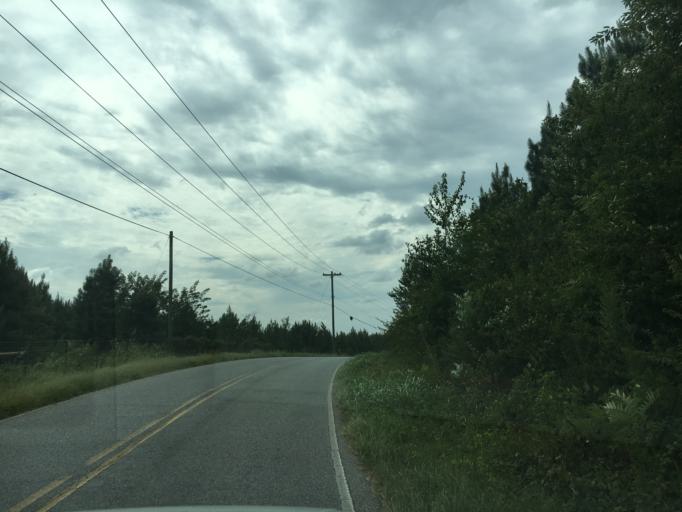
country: US
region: South Carolina
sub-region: Greenville County
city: Greer
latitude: 34.9255
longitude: -82.1975
